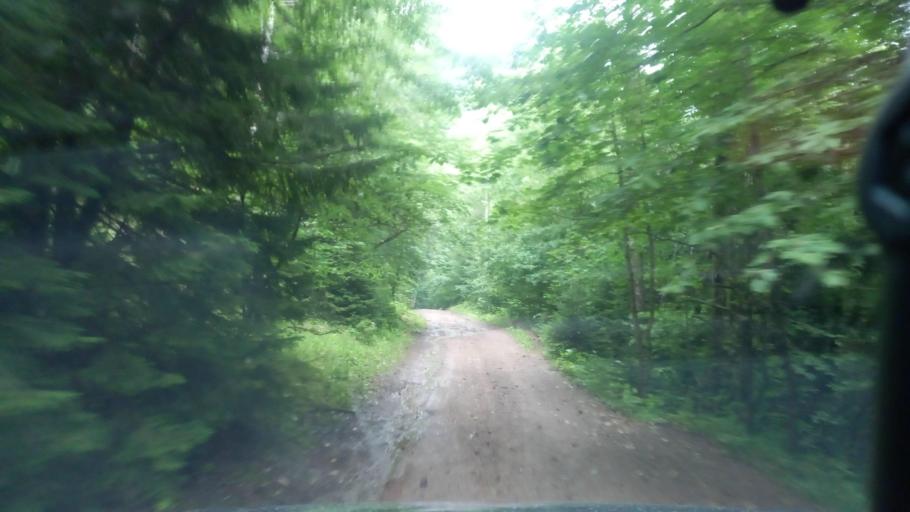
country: RU
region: Karachayevo-Cherkesiya
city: Kurdzhinovo
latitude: 43.8114
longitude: 40.8700
